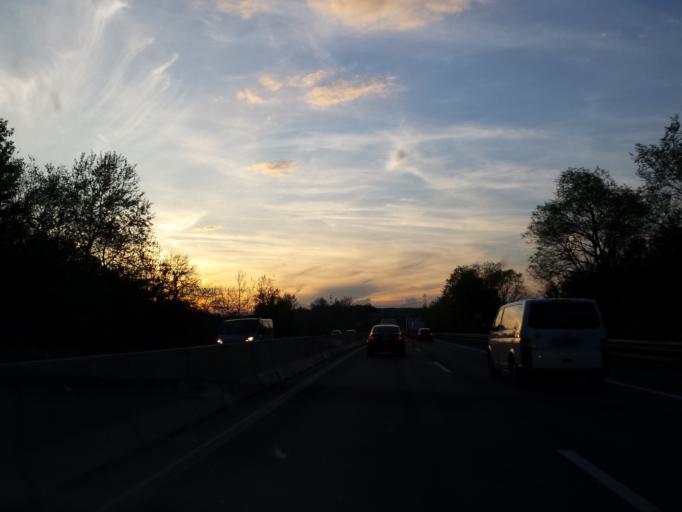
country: AT
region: Lower Austria
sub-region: Politischer Bezirk Bruck an der Leitha
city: Trautmannsdorf an der Leitha
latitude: 48.0636
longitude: 16.6983
